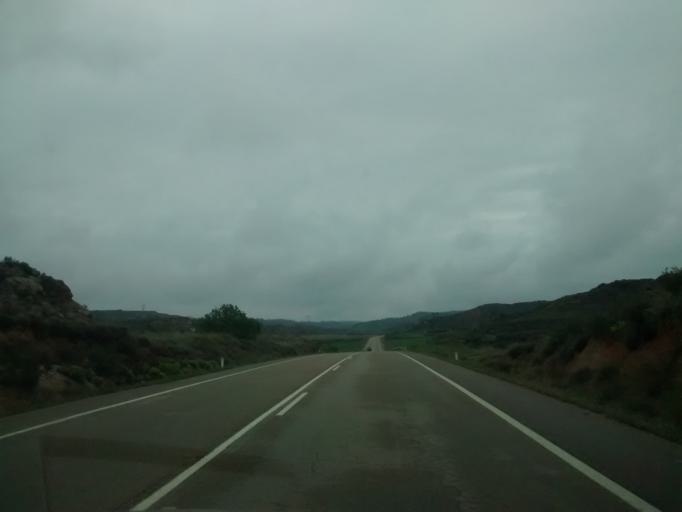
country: ES
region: Aragon
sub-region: Provincia de Zaragoza
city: Caspe
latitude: 41.2080
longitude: 0.0189
